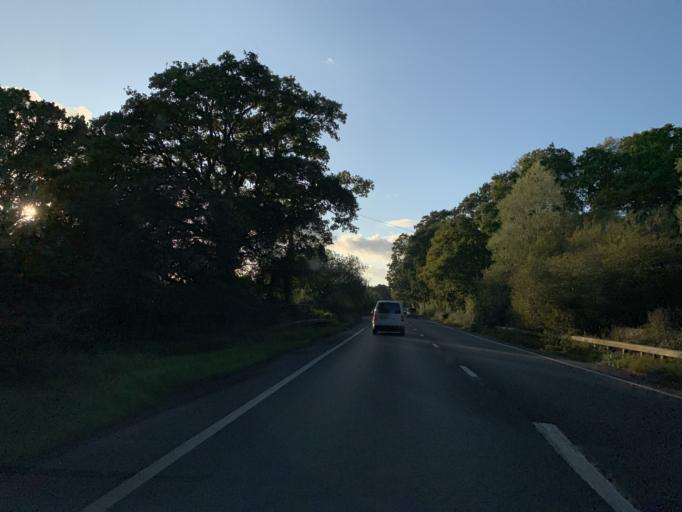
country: GB
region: England
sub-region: Hampshire
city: West Wellow
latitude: 50.9749
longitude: -1.6188
